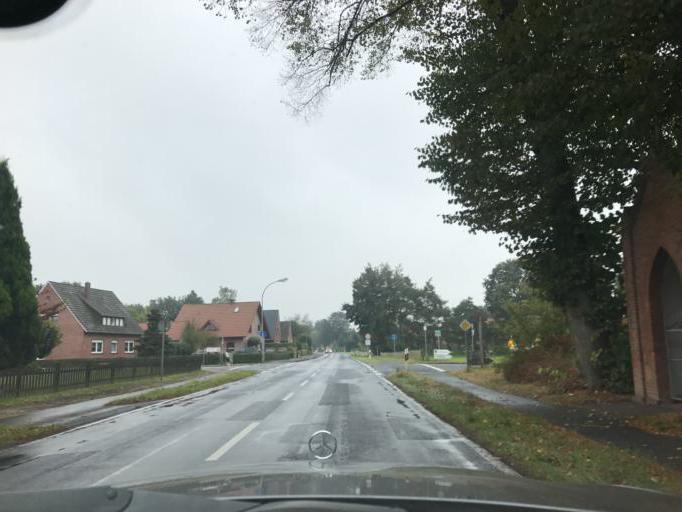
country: DE
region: Lower Saxony
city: Lehe
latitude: 53.0622
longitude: 7.3382
